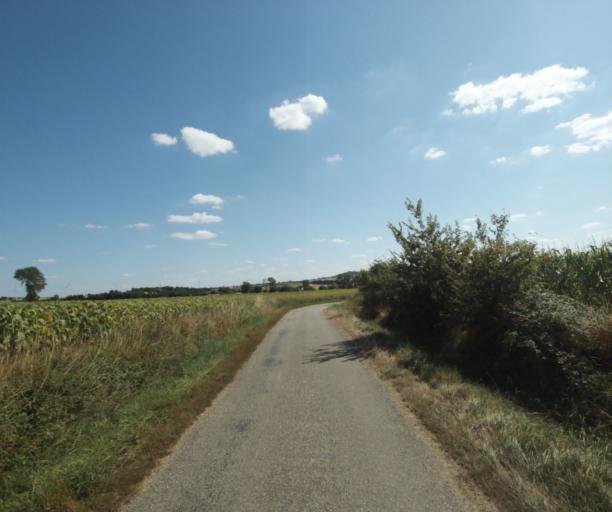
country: FR
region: Midi-Pyrenees
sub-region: Departement de la Haute-Garonne
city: Saint-Felix-Lauragais
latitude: 43.4789
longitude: 1.8956
